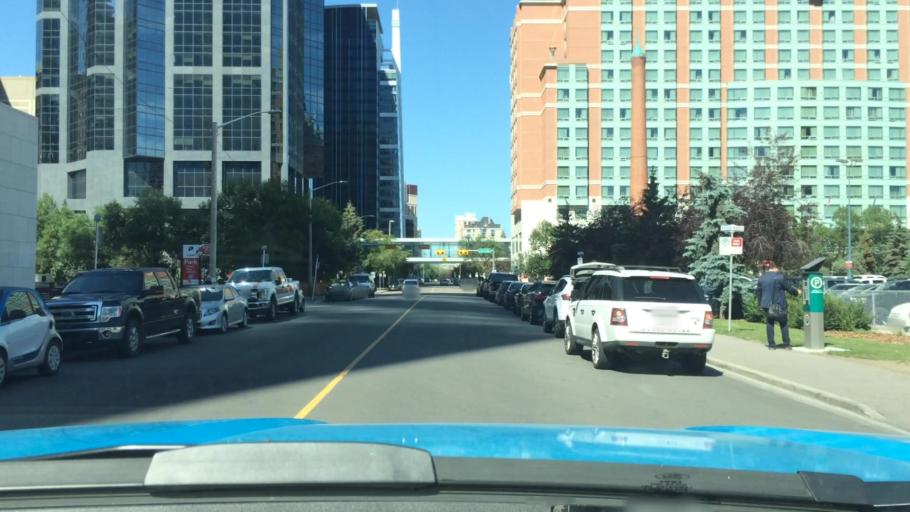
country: CA
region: Alberta
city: Calgary
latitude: 51.0514
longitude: -114.0685
